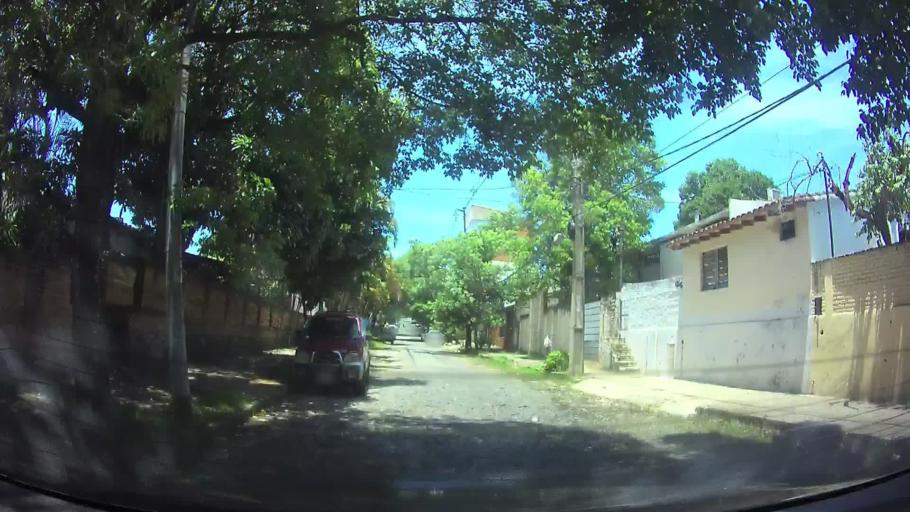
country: PY
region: Asuncion
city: Asuncion
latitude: -25.2814
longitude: -57.6053
